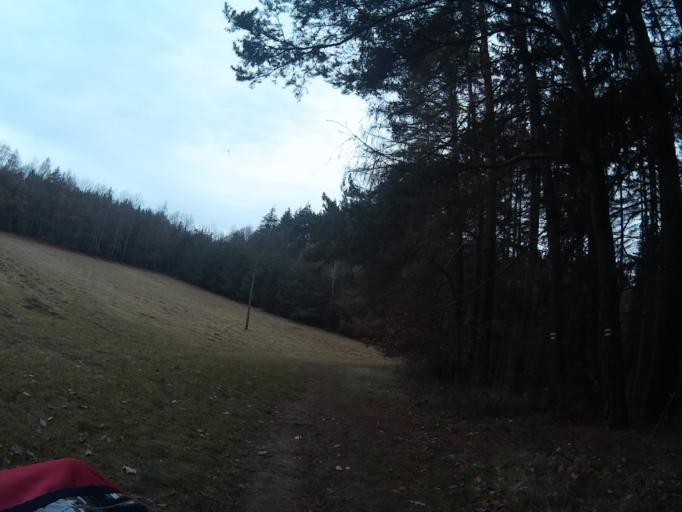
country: CZ
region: Plzensky
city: Stary Plzenec
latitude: 49.6814
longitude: 13.4786
